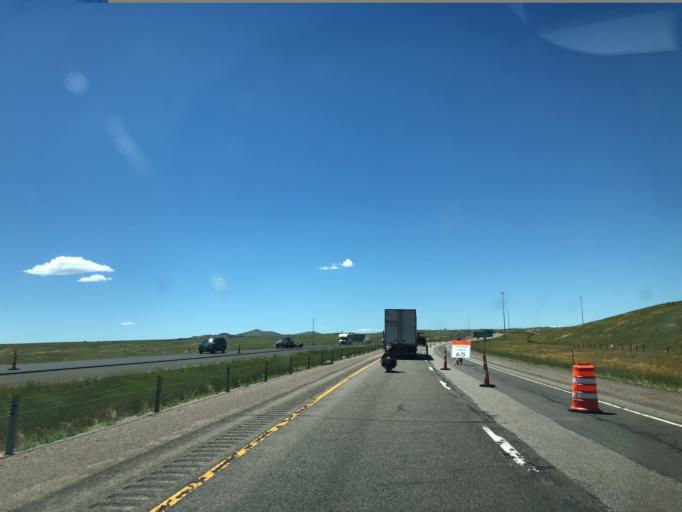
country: US
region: Wyoming
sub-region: Laramie County
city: Cheyenne
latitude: 41.0973
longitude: -105.1058
